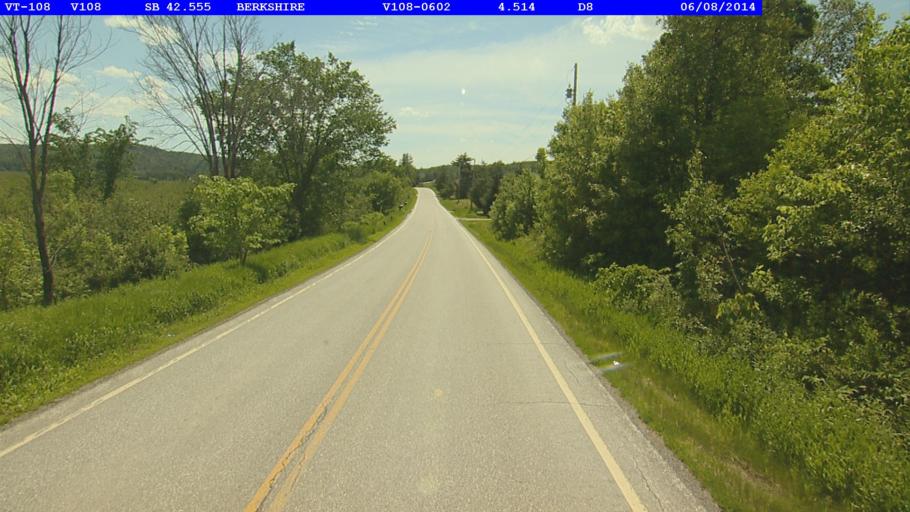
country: US
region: Vermont
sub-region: Franklin County
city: Enosburg Falls
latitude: 44.9862
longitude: -72.8170
